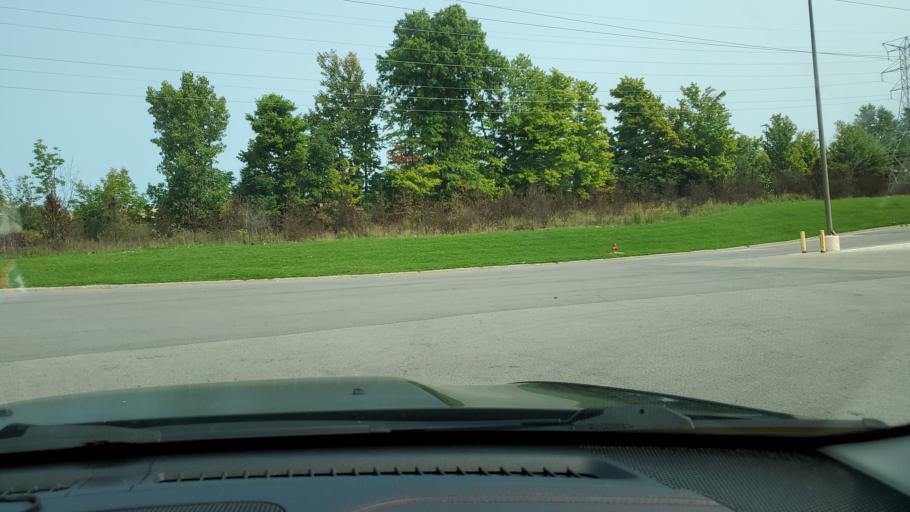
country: US
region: Ohio
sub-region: Mahoning County
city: Poland
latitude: 41.0320
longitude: -80.6342
